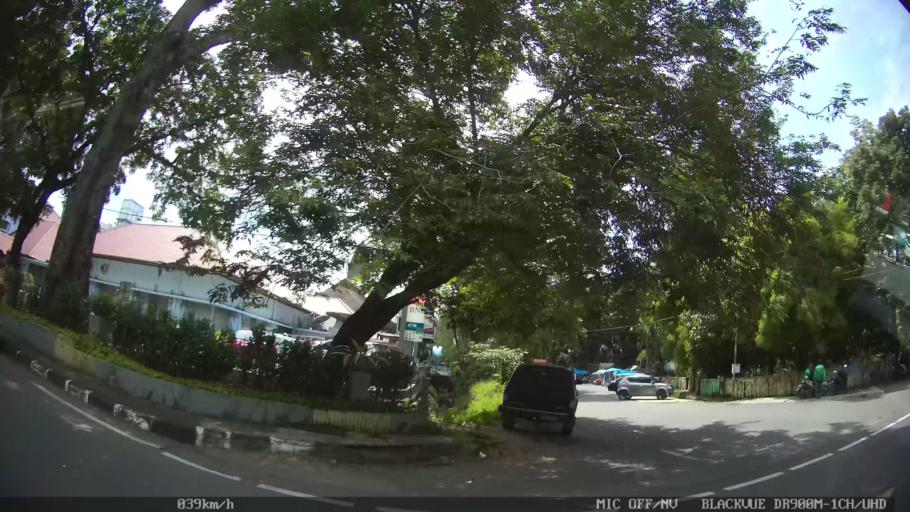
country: ID
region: North Sumatra
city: Medan
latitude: 3.5754
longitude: 98.6773
